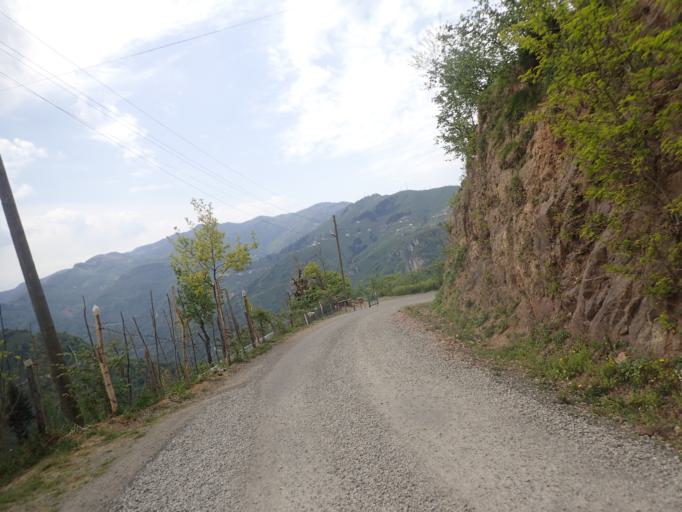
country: TR
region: Ordu
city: Kabaduz
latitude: 40.7954
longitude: 37.8891
